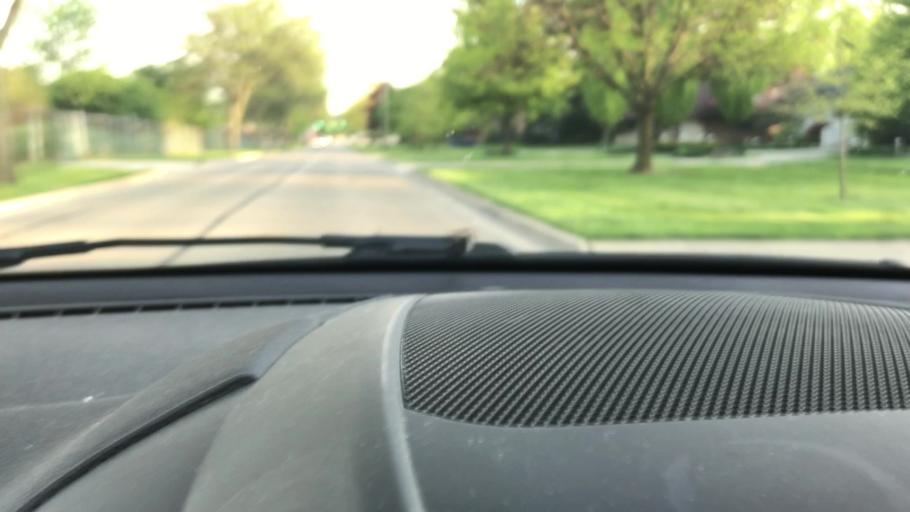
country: US
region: Michigan
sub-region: Oakland County
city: Huntington Woods
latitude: 42.4773
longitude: -83.1729
